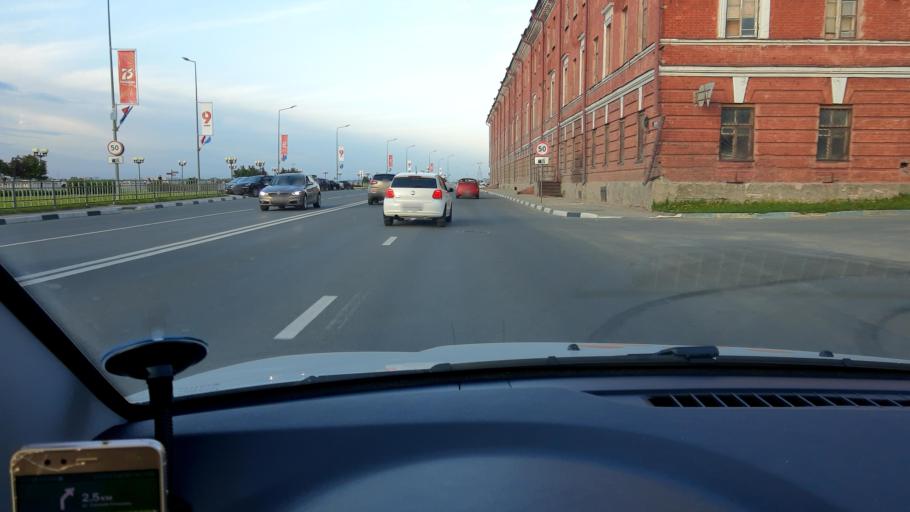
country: RU
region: Nizjnij Novgorod
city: Nizhniy Novgorod
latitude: 56.3329
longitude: 44.0052
